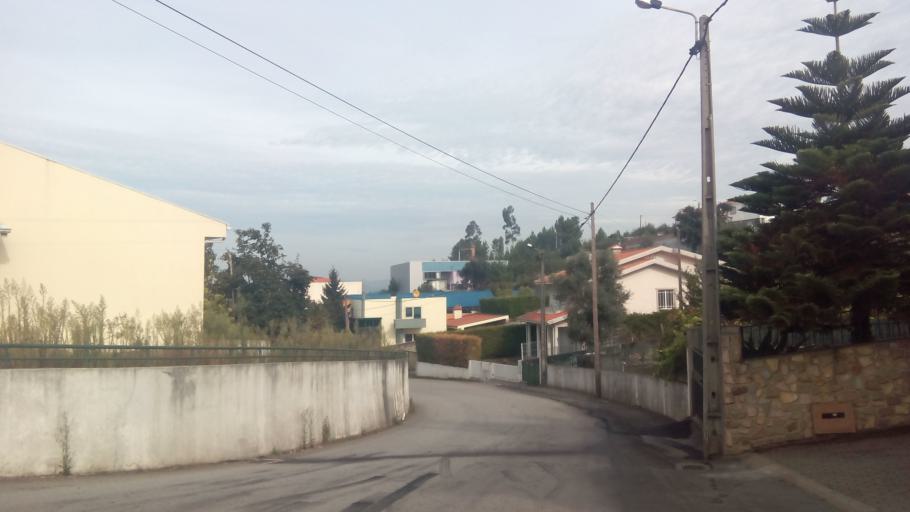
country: PT
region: Porto
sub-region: Paredes
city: Gandra
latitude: 41.1812
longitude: -8.4364
